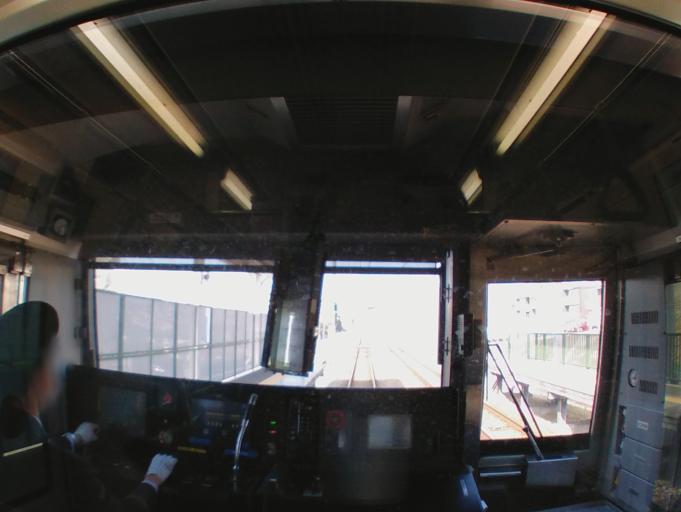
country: JP
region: Tokyo
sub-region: Machida-shi
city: Machida
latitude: 35.6058
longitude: 139.4814
